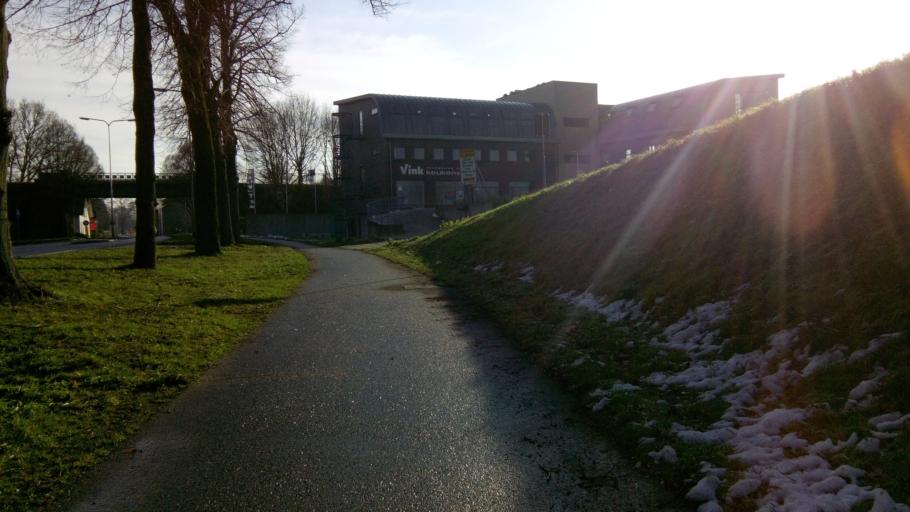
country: NL
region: North Brabant
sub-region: Gemeente Cuijk
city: Cuijk
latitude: 51.7582
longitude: 5.8714
